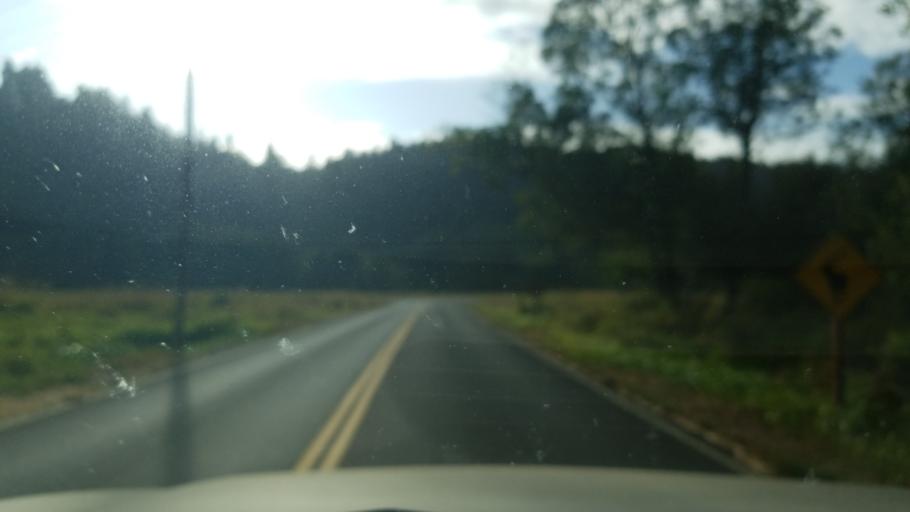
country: US
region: California
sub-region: Humboldt County
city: Westhaven-Moonstone
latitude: 41.3213
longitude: -124.0407
